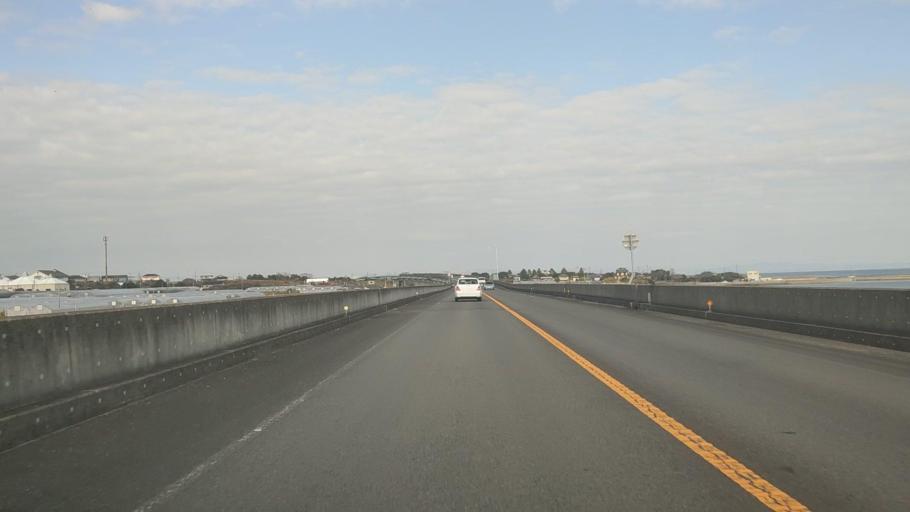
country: JP
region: Nagasaki
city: Shimabara
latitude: 32.7329
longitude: 130.3680
